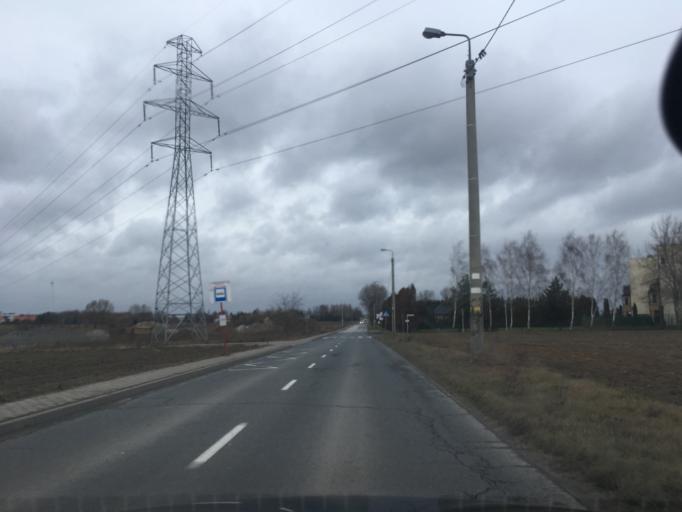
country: PL
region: Masovian Voivodeship
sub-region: Powiat piaseczynski
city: Lesznowola
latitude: 52.0952
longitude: 20.9338
